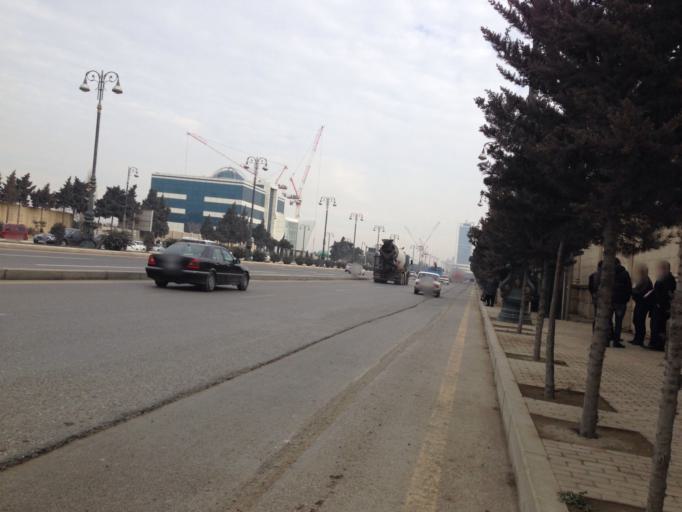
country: AZ
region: Baki
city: Baku
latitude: 40.4073
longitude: 49.8899
